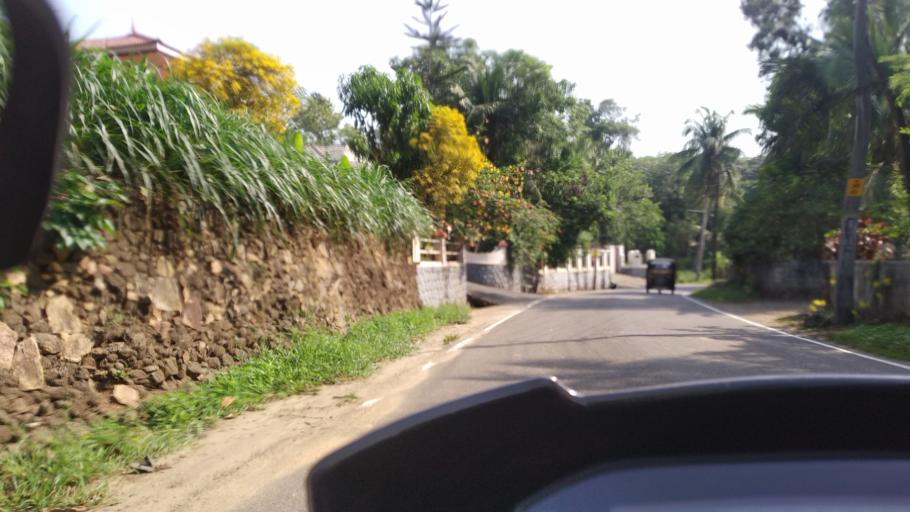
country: IN
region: Kerala
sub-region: Ernakulam
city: Piravam
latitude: 9.8118
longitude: 76.5643
